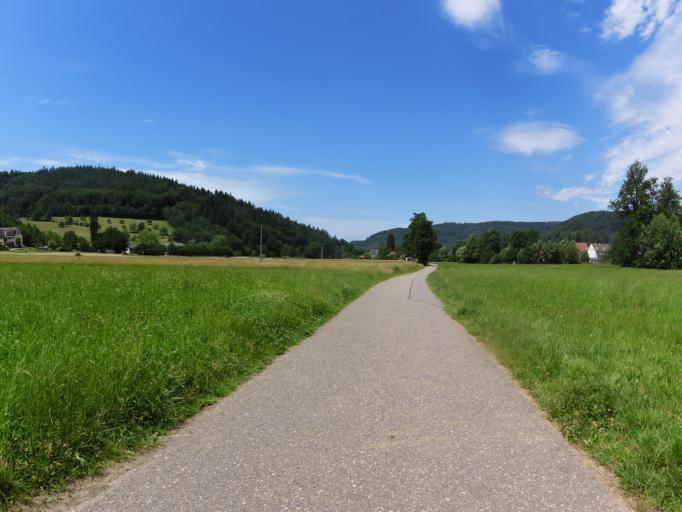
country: DE
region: Baden-Wuerttemberg
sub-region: Freiburg Region
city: Seelbach
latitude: 48.3261
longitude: 7.9276
